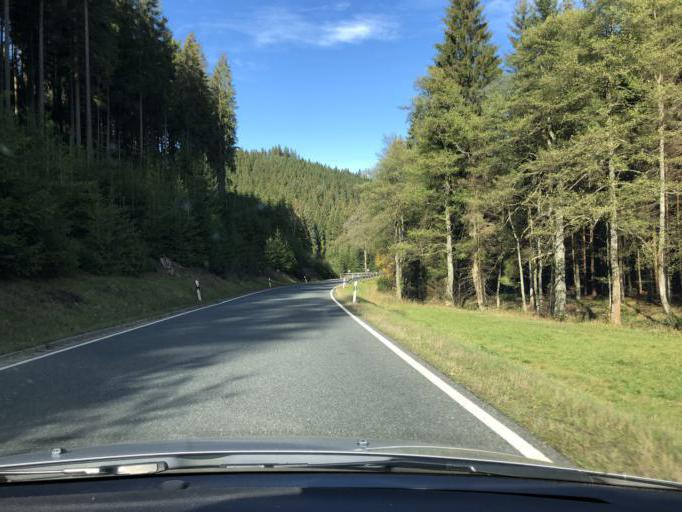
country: DE
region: Thuringia
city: Katzhutte
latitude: 50.5338
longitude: 11.0898
